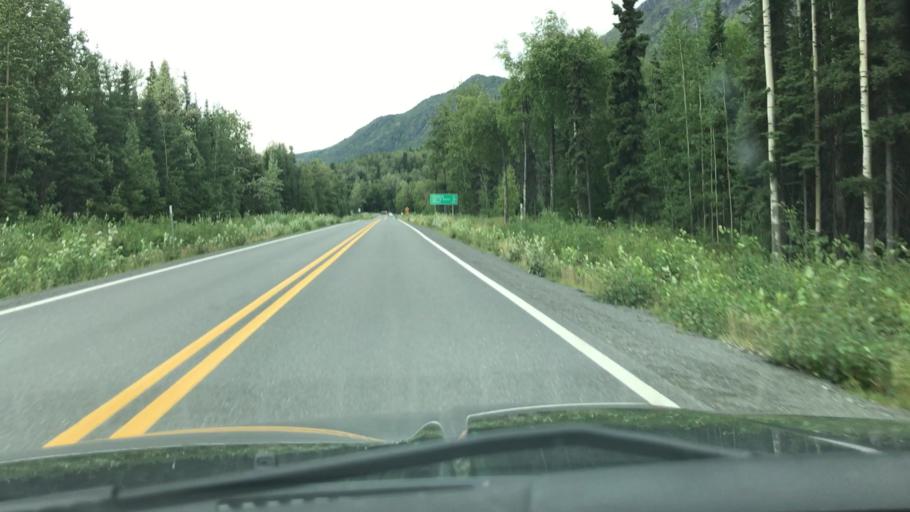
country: US
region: Alaska
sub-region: Kenai Peninsula Borough
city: Seward
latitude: 60.4870
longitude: -149.9696
